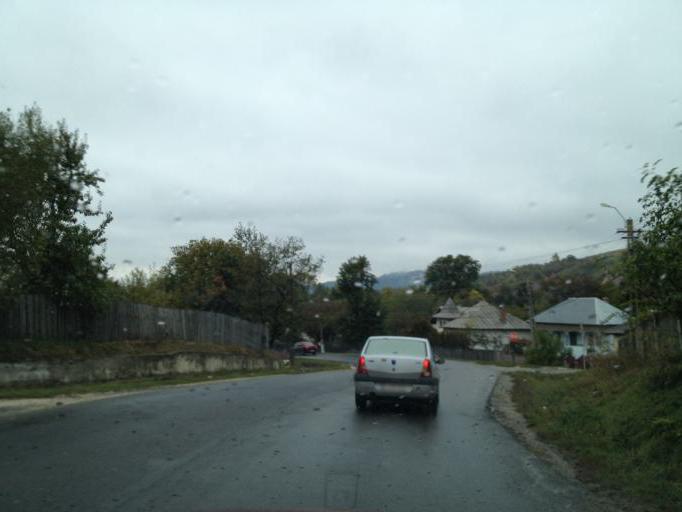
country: RO
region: Arges
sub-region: Comuna Valea Mare-Pravat
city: Valea Mare Pravat
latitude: 45.2961
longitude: 25.1042
